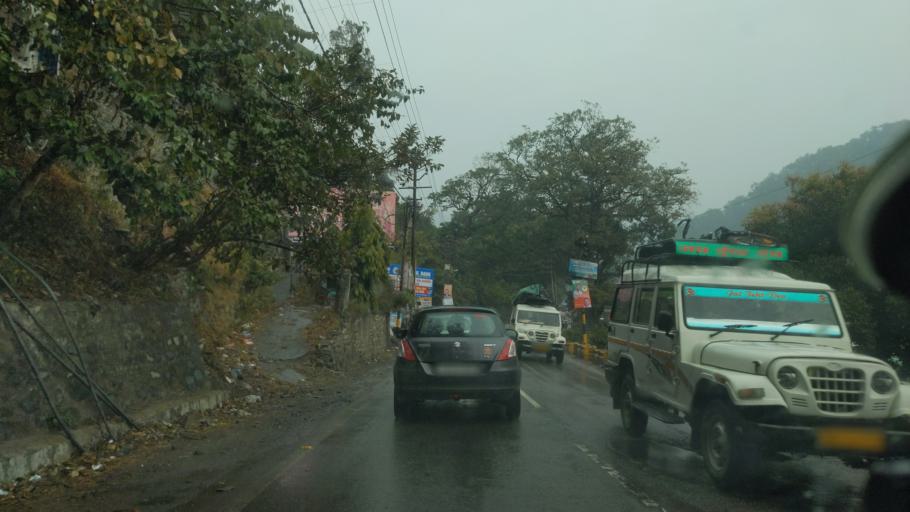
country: IN
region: Uttarakhand
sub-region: Naini Tal
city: Bhim Tal
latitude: 29.2845
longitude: 79.5463
